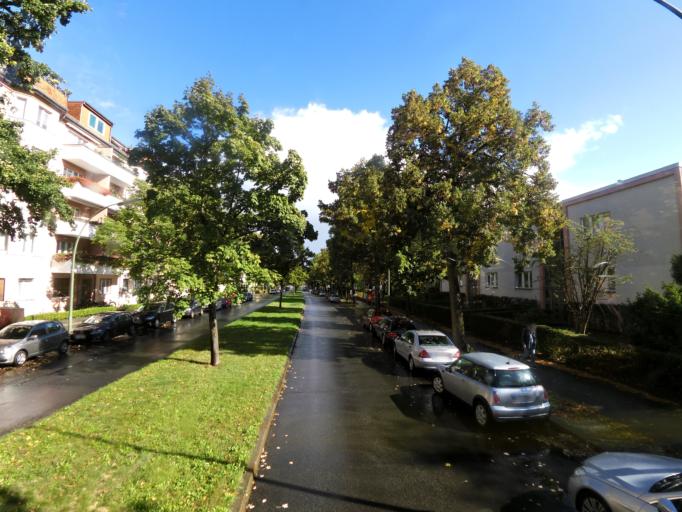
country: DE
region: Berlin
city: Schmargendorf
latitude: 52.4761
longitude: 13.2848
